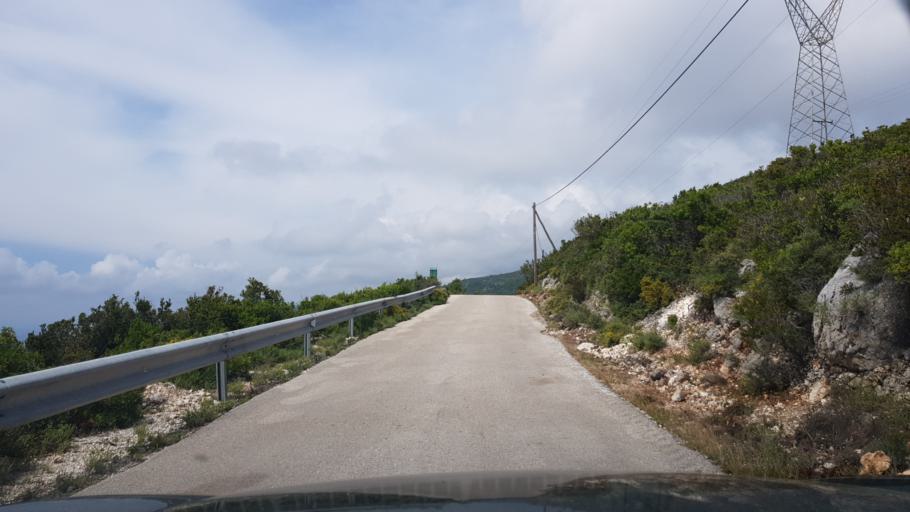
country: GR
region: Ionian Islands
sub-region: Lefkada
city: Nidri
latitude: 38.6027
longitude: 20.5593
